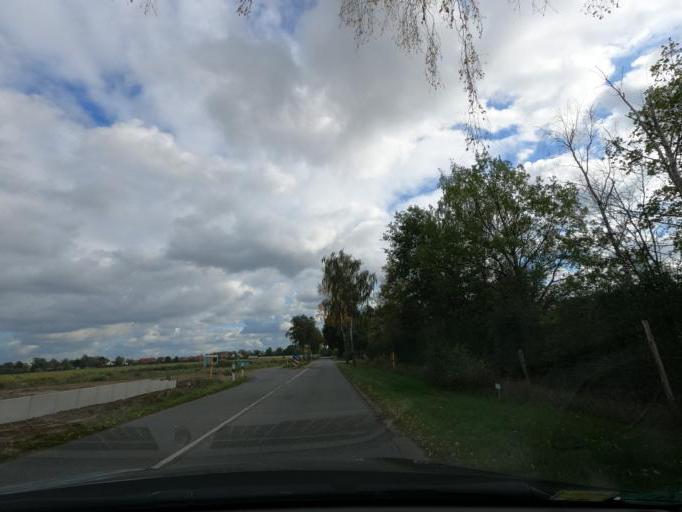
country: DE
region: Lower Saxony
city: Klein Schwulper
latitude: 52.3456
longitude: 10.4468
